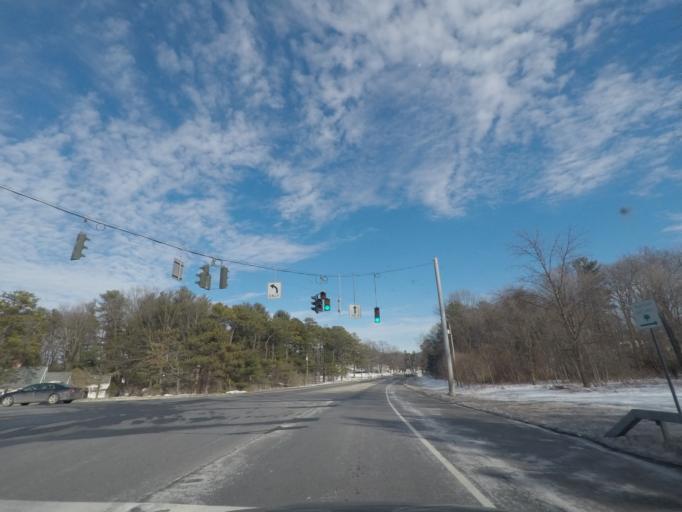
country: US
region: New York
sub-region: Schenectady County
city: Rotterdam
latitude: 42.7877
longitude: -74.0102
